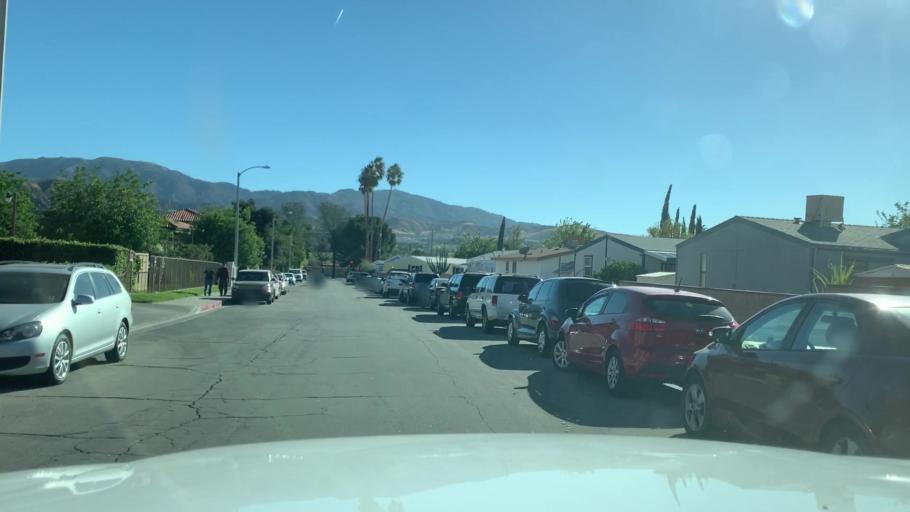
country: US
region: California
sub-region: Los Angeles County
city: Santa Clarita
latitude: 34.4181
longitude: -118.4524
